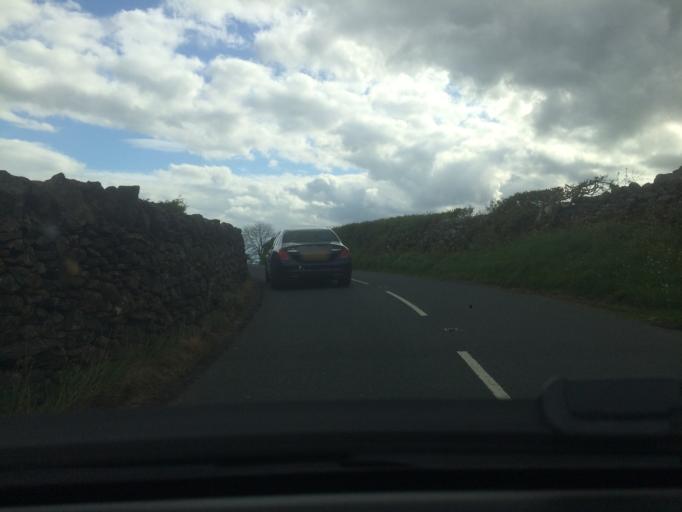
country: GB
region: England
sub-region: Cumbria
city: Windermere
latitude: 54.4242
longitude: -2.9055
